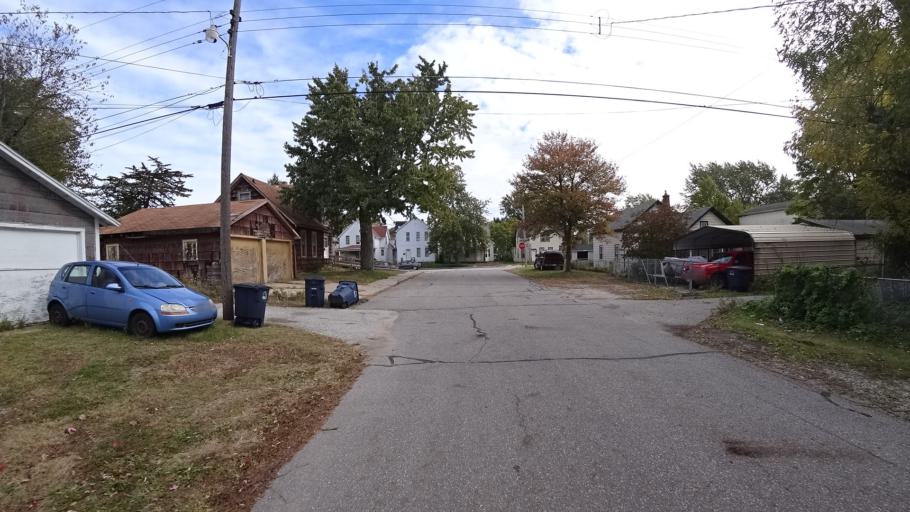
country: US
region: Indiana
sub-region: LaPorte County
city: Michigan City
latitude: 41.7088
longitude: -86.9053
